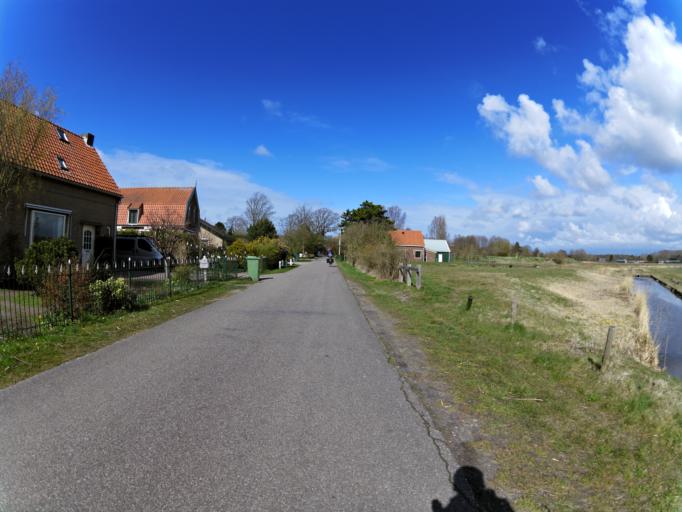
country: NL
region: South Holland
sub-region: Gemeente Hellevoetsluis
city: Nieuw-Helvoet
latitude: 51.8865
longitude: 4.0594
